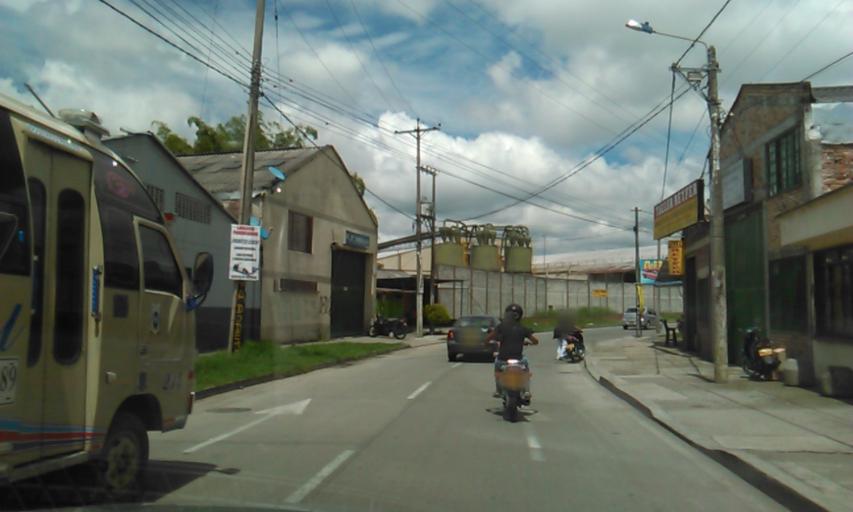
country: CO
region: Quindio
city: Armenia
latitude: 4.5166
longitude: -75.6893
